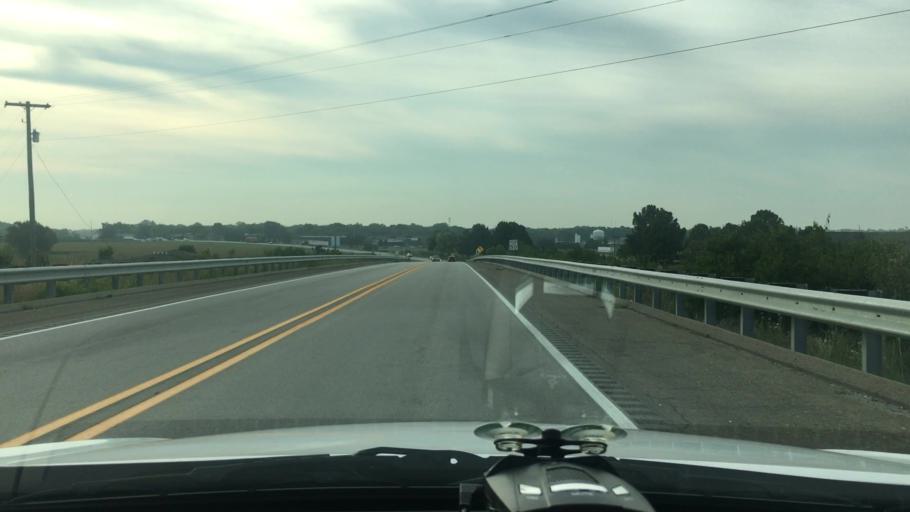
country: US
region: Illinois
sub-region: Champaign County
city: Champaign
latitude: 40.1423
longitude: -88.2864
